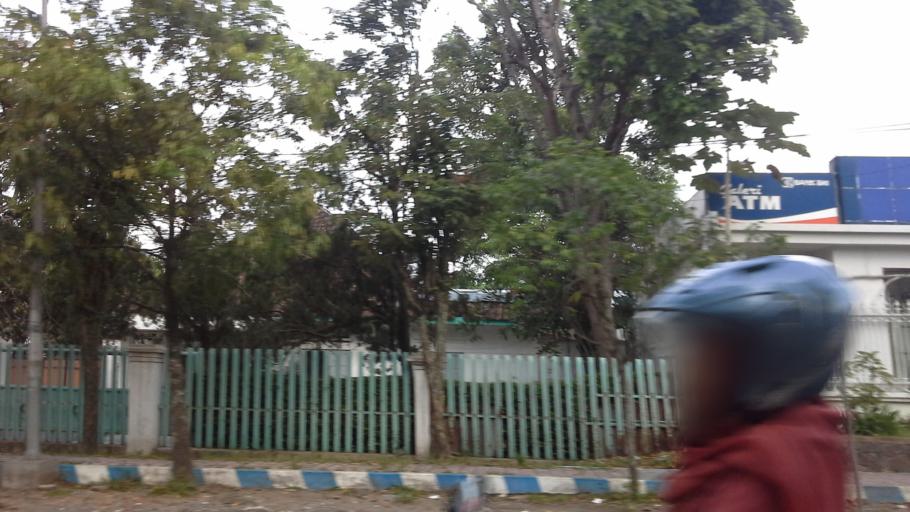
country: ID
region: East Java
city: Bondowoso
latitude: -7.9203
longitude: 113.8278
